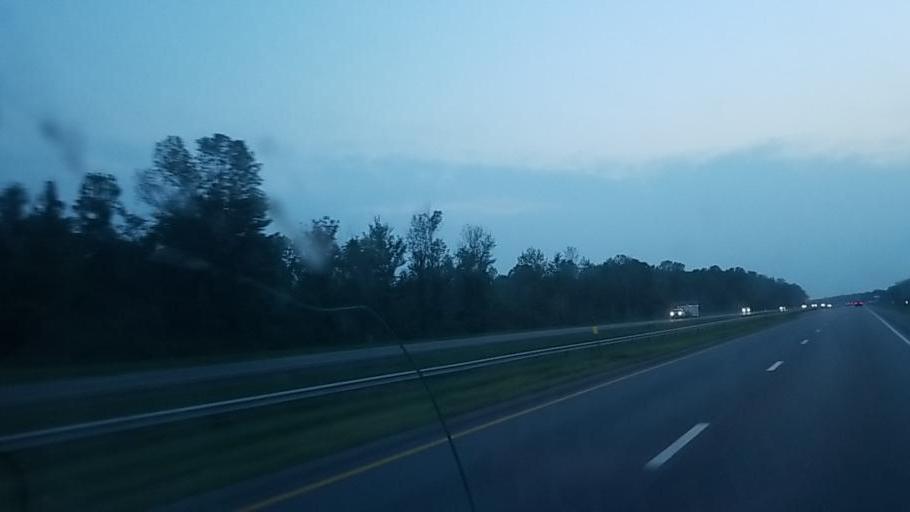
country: US
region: New York
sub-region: Madison County
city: Canastota
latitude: 43.0929
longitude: -75.7903
